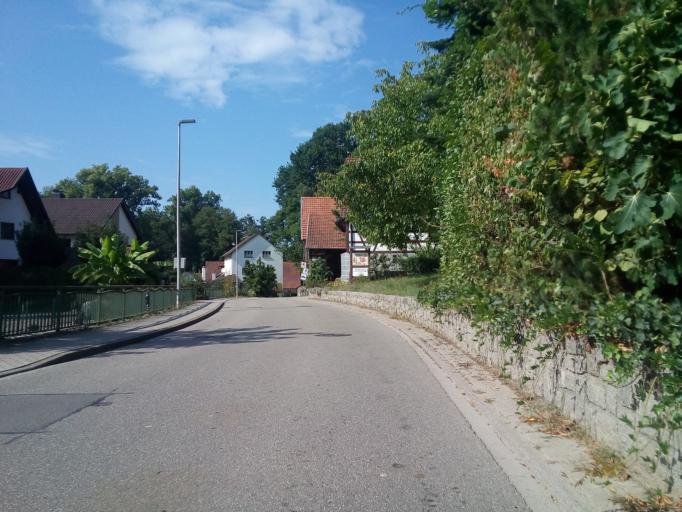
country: DE
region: Baden-Wuerttemberg
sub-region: Karlsruhe Region
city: Ottersweier
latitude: 48.6582
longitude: 8.1166
